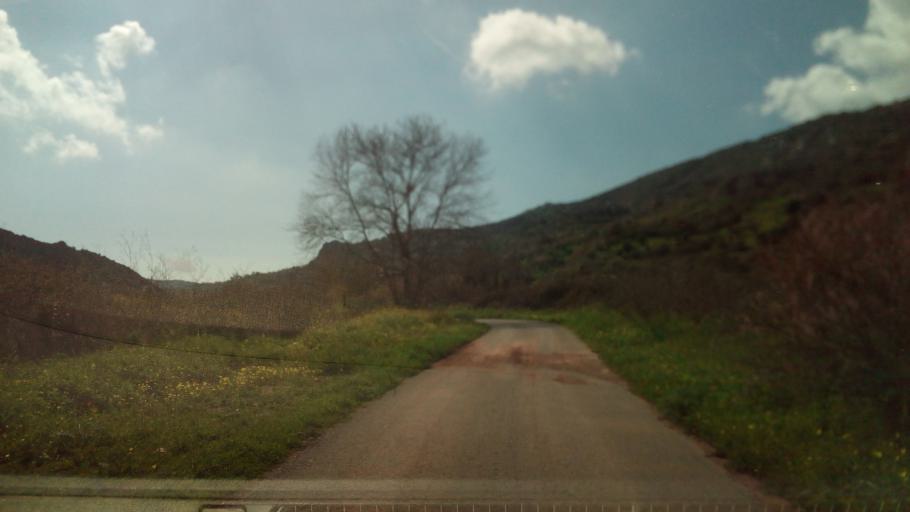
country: CY
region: Pafos
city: Mesogi
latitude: 34.8050
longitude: 32.5311
